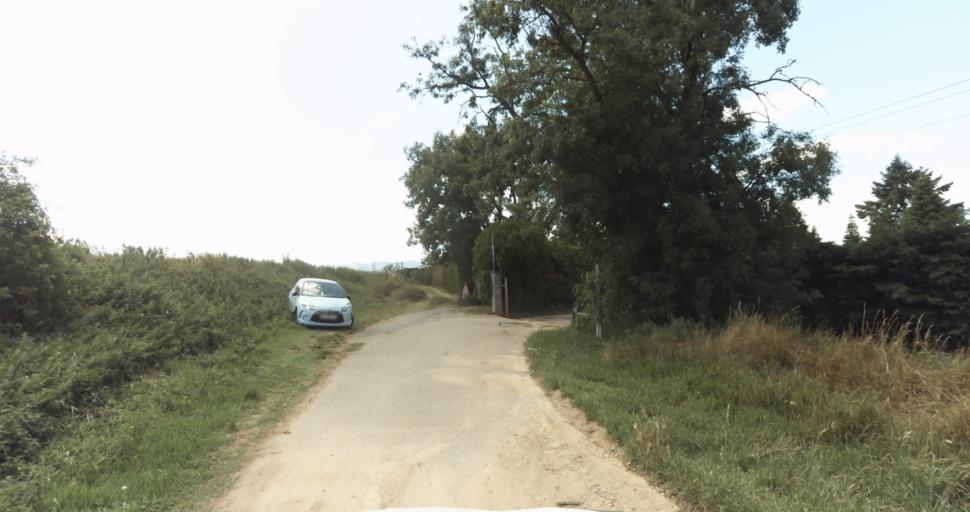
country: FR
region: Rhone-Alpes
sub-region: Departement du Rhone
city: Francheville
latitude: 45.7263
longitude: 4.7607
